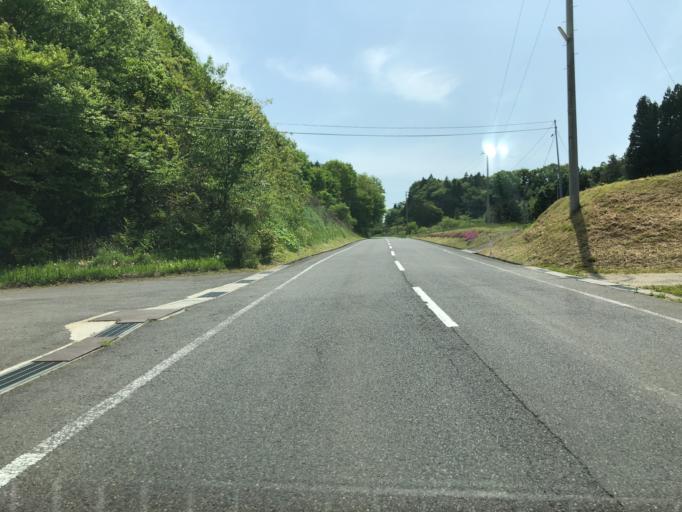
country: JP
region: Fukushima
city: Ishikawa
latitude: 37.1891
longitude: 140.5350
